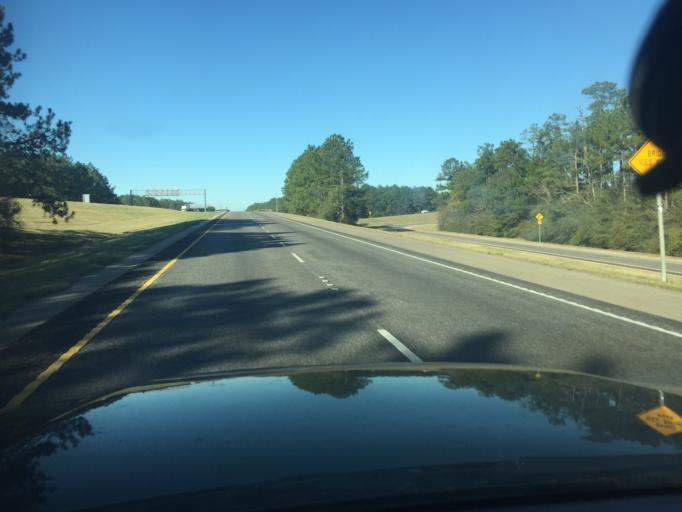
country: US
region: Louisiana
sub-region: Saint Tammany Parish
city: Slidell
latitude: 30.3054
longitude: -89.7376
